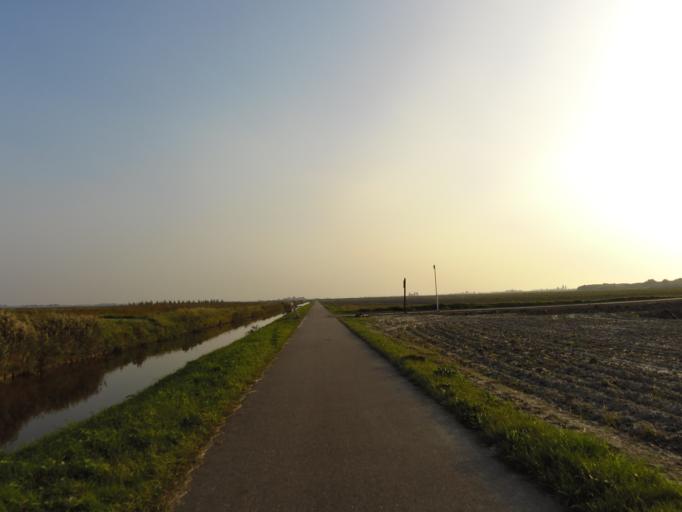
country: NL
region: South Holland
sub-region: Gemeente Waddinxveen
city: Groenswaard
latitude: 52.0730
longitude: 4.6069
